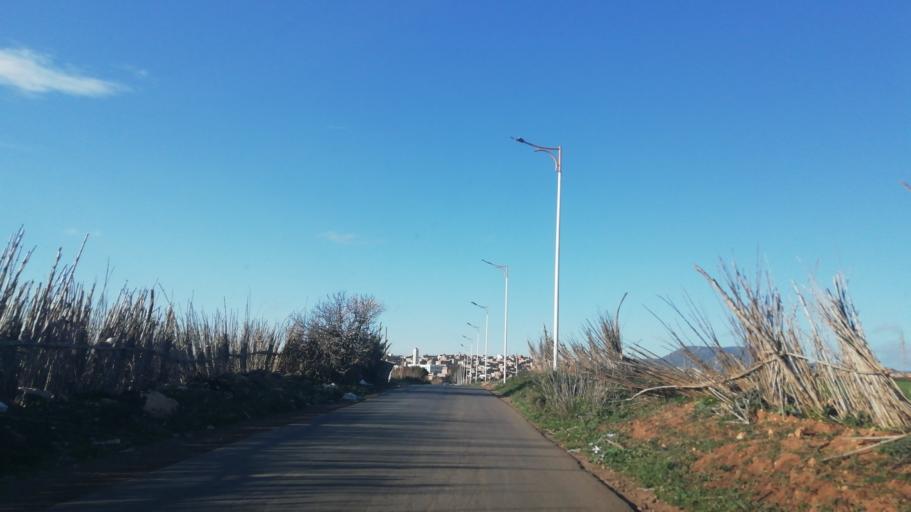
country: DZ
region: Oran
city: Sidi ech Chahmi
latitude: 35.6835
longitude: -0.4934
